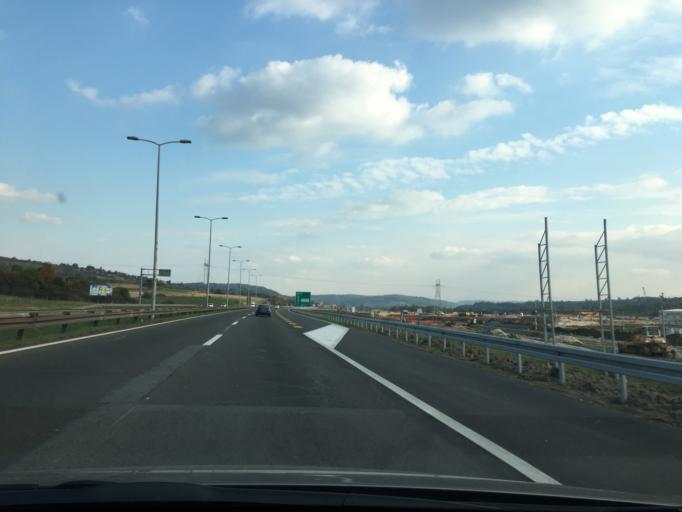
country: RS
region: Central Serbia
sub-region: Belgrade
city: Zvezdara
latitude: 44.7147
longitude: 20.5602
